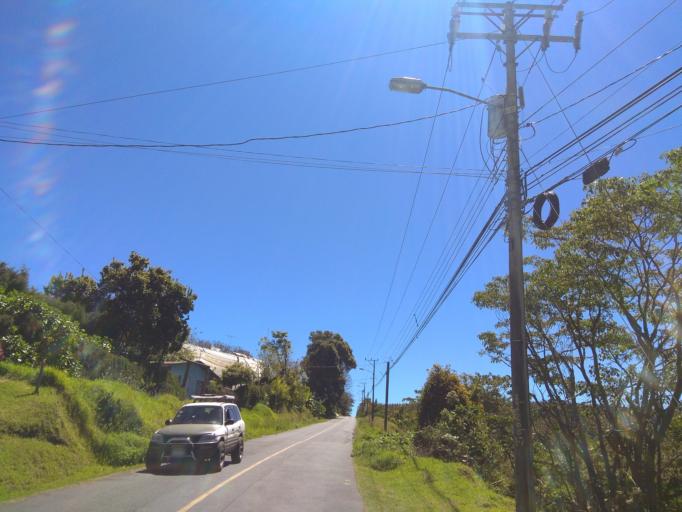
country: CR
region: Cartago
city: Cot
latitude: 9.9452
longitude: -83.9183
